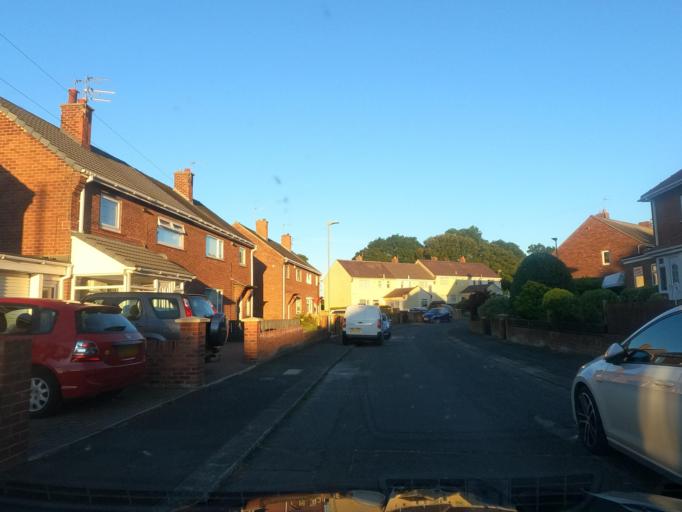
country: GB
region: England
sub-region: Northumberland
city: Newbiggin-by-the-Sea
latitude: 55.1795
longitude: -1.5217
